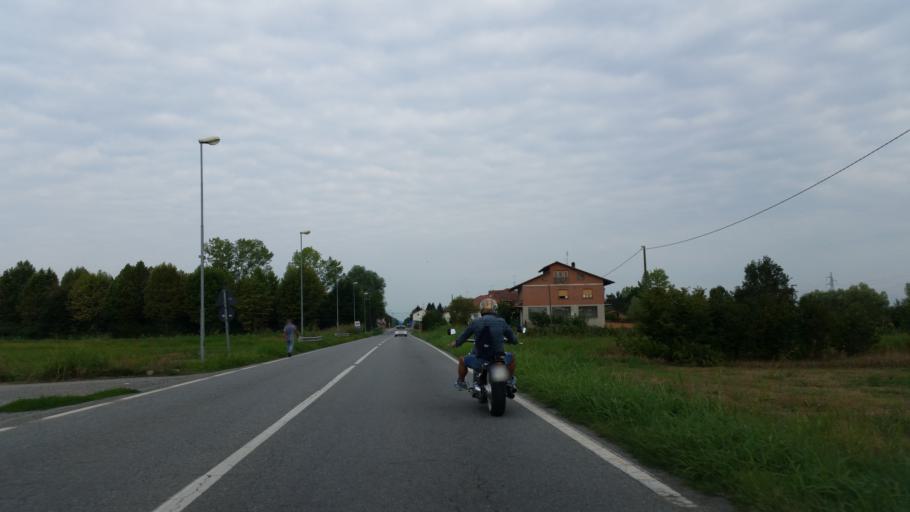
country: IT
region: Piedmont
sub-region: Provincia di Torino
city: Monteu da Po
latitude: 45.1595
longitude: 8.0254
